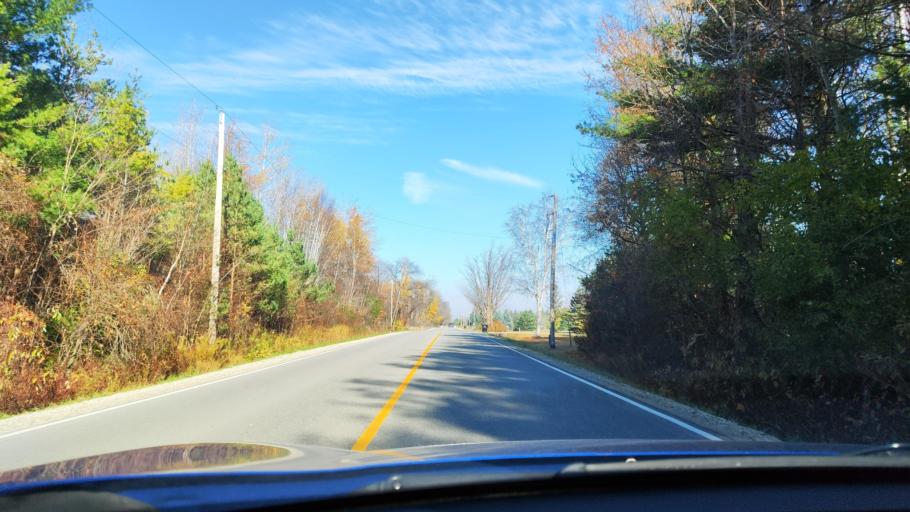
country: CA
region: Ontario
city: Wasaga Beach
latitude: 44.4080
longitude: -80.0596
